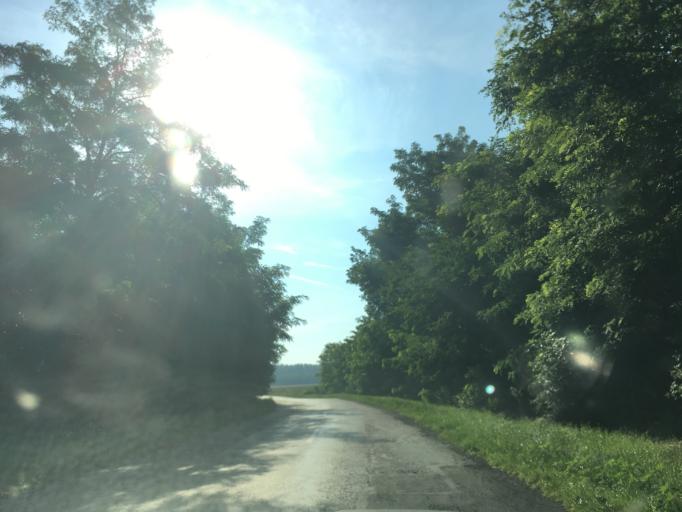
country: HU
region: Hajdu-Bihar
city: Nyiradony
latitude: 47.6911
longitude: 21.9615
